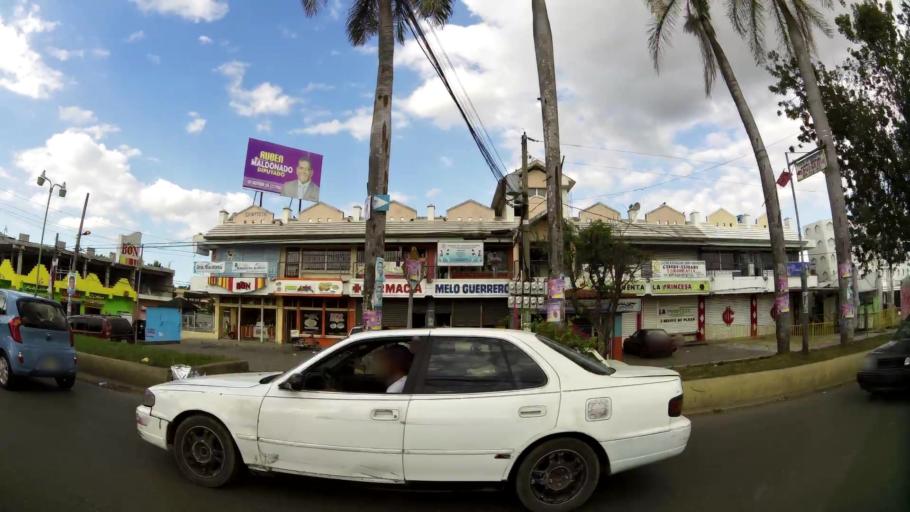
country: DO
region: Nacional
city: Ensanche Luperon
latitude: 18.5526
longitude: -69.9025
